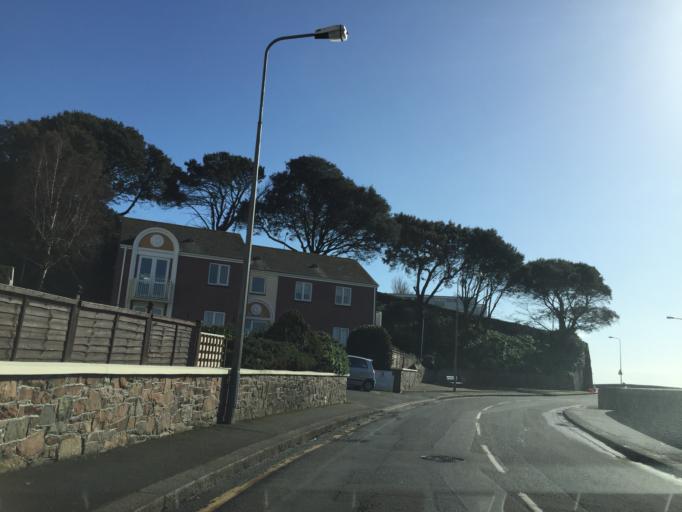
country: JE
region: St Helier
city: Saint Helier
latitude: 49.1787
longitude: -2.1086
